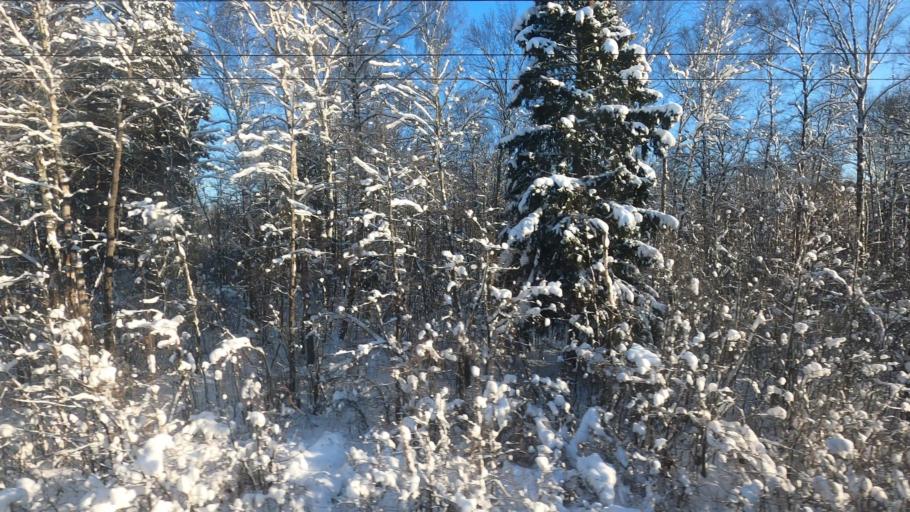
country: RU
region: Moskovskaya
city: Zhukovka
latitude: 56.4631
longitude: 37.5260
